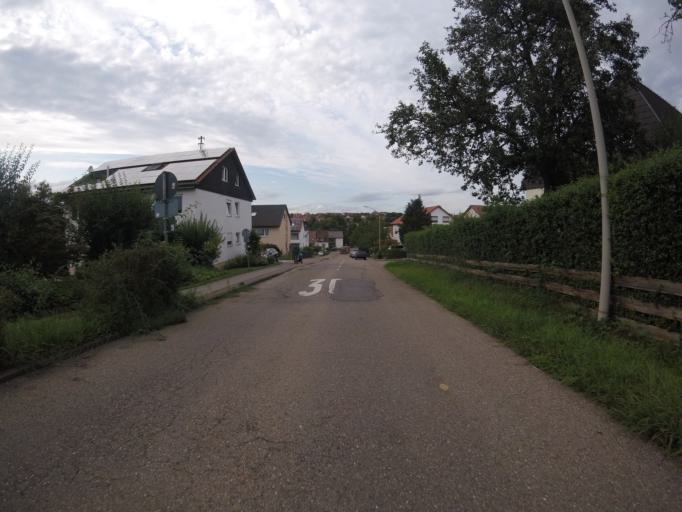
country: DE
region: Baden-Wuerttemberg
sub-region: Regierungsbezirk Stuttgart
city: Backnang
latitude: 48.9213
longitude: 9.4270
